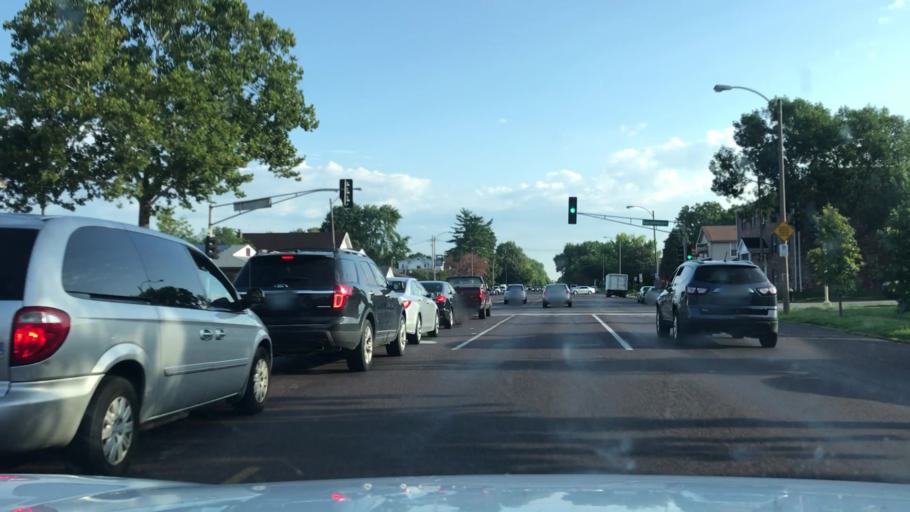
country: US
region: Missouri
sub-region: Saint Louis County
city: Maplewood
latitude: 38.5910
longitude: -90.3099
